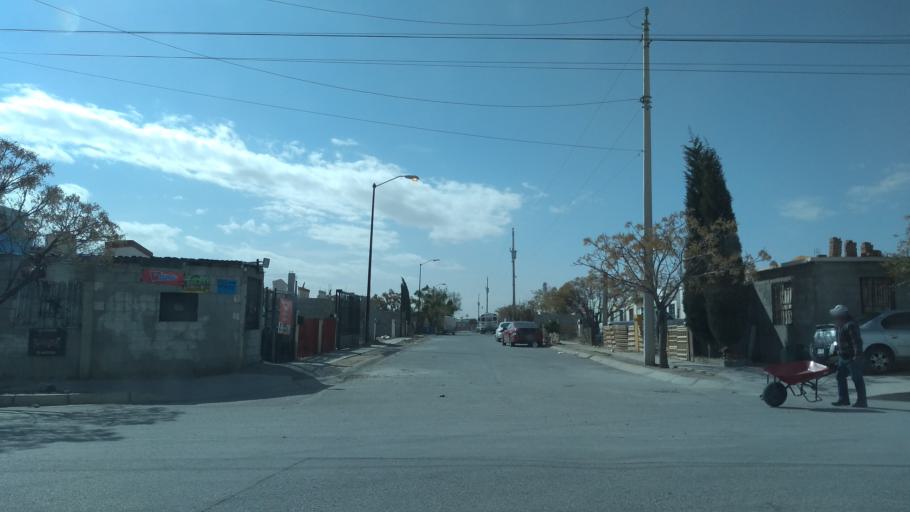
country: US
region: Texas
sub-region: El Paso County
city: San Elizario
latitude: 31.5626
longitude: -106.3351
